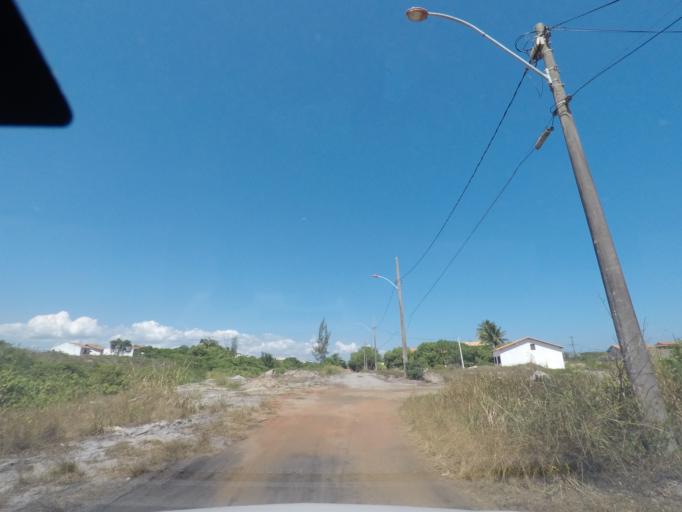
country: BR
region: Rio de Janeiro
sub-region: Marica
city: Marica
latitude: -22.9720
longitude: -42.9174
